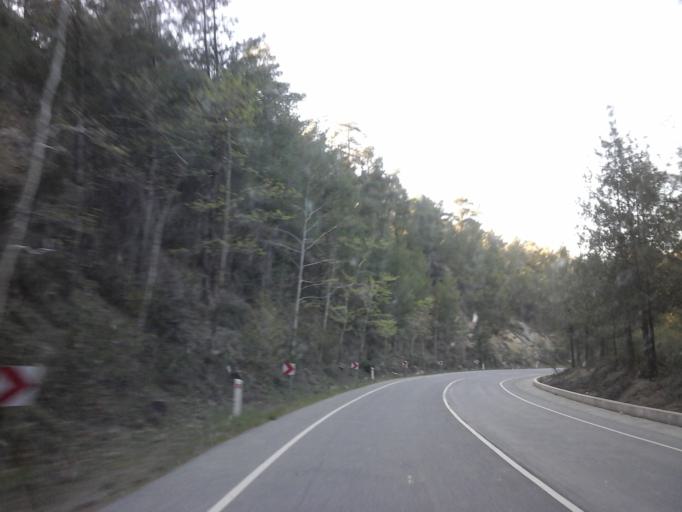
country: CY
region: Lefkosia
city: Kakopetria
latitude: 34.9578
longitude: 32.9228
